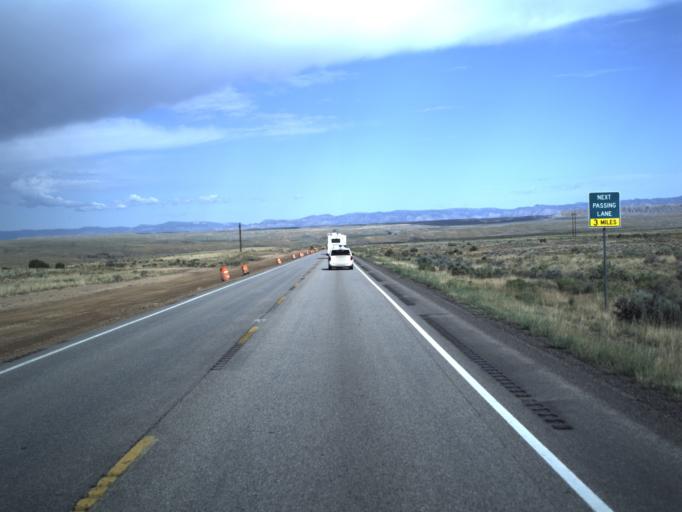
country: US
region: Utah
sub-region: Carbon County
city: East Carbon City
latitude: 39.4428
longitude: -110.4661
